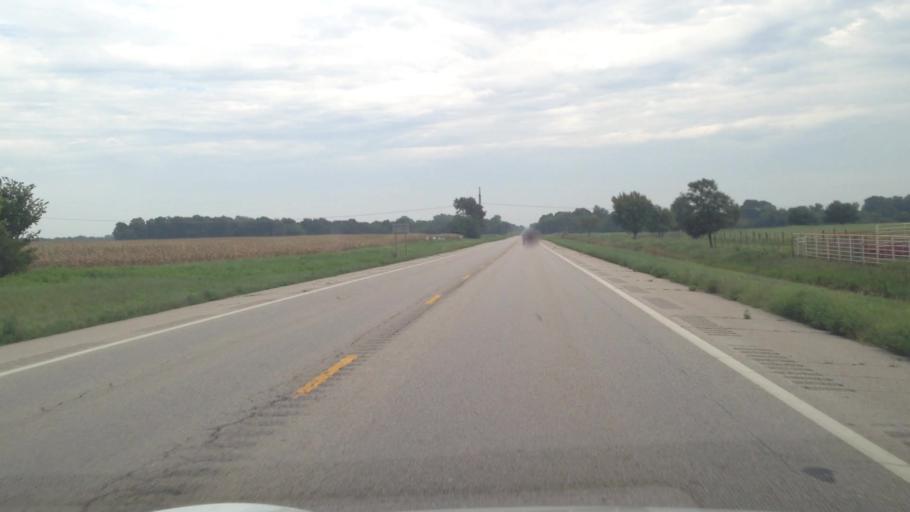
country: US
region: Kansas
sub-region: Crawford County
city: Pittsburg
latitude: 37.3393
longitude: -94.7959
